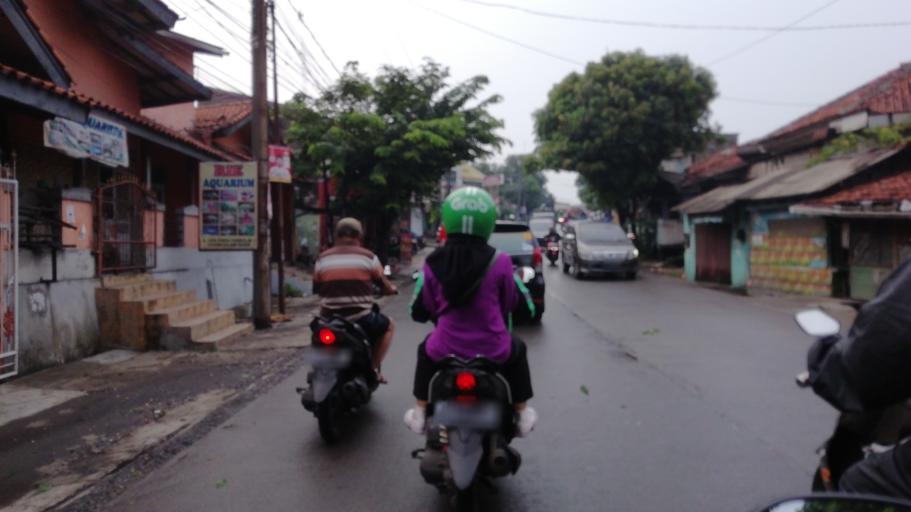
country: ID
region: West Java
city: Bogor
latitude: -6.5529
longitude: 106.8077
